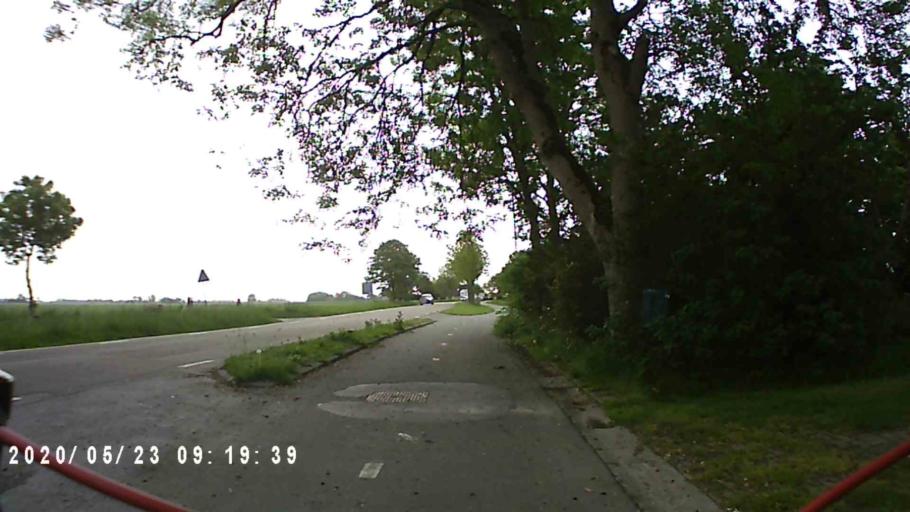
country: NL
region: Groningen
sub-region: Gemeente Bedum
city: Bedum
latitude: 53.2974
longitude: 6.6688
